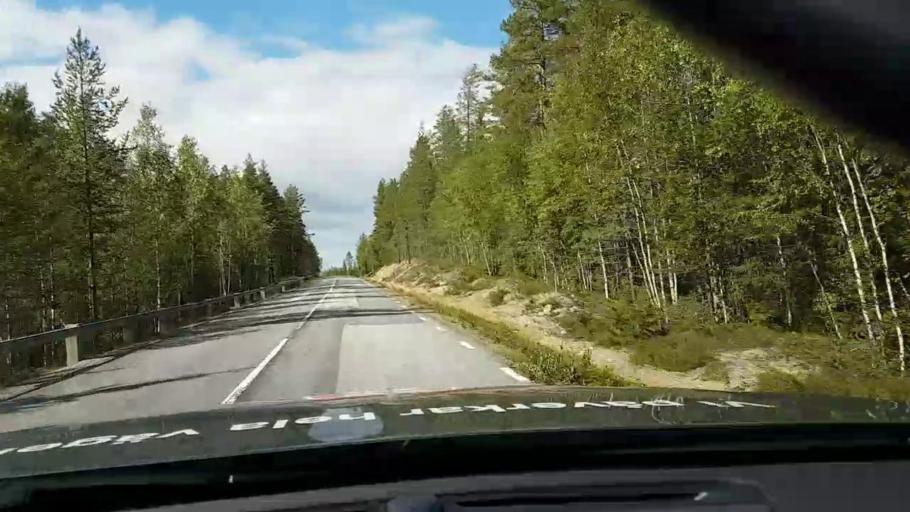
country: SE
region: Vaesterbotten
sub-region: Asele Kommun
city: Asele
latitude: 63.8403
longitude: 17.4297
